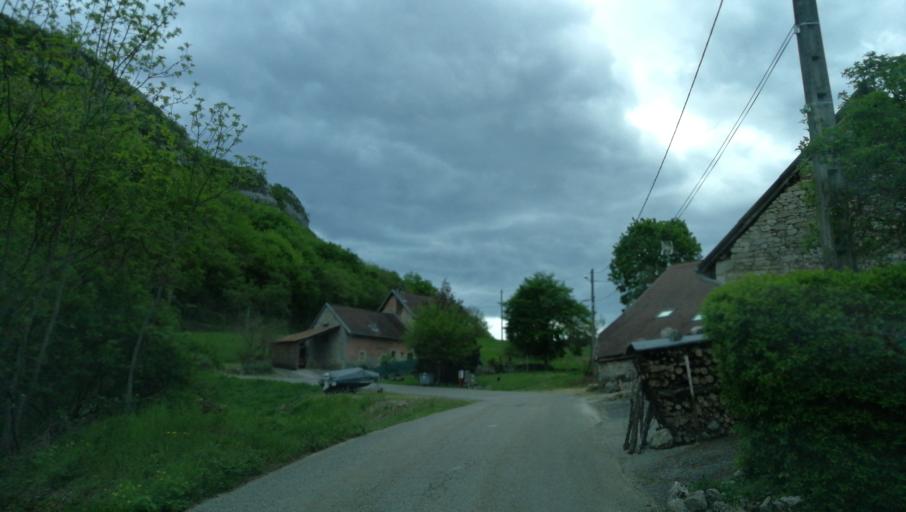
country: FR
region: Rhone-Alpes
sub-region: Departement de la Savoie
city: Chatillon
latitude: 45.7740
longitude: 5.8198
